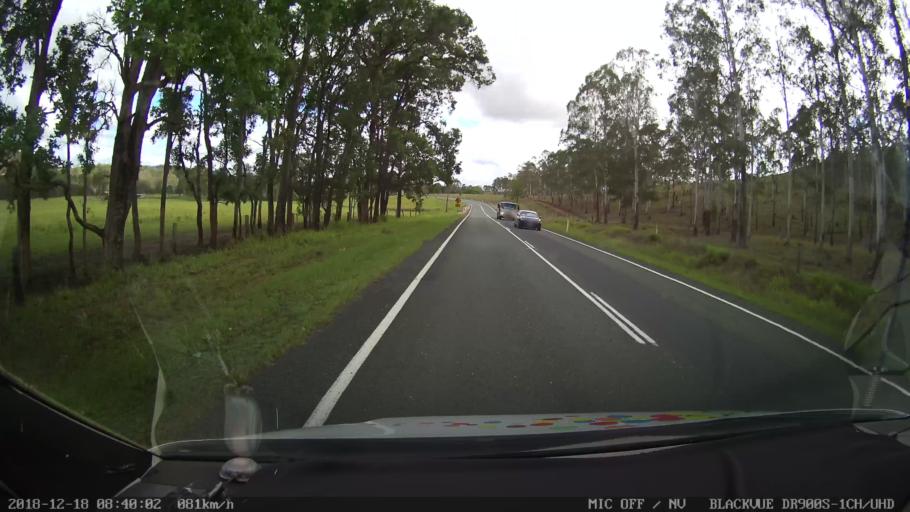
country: AU
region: Queensland
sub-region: Logan
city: Cedar Vale
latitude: -28.2462
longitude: 152.8445
